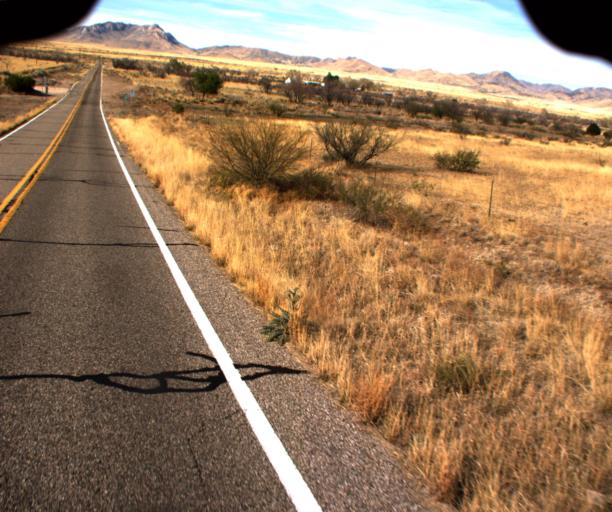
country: US
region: Arizona
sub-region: Cochise County
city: Willcox
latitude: 32.0122
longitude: -109.4400
